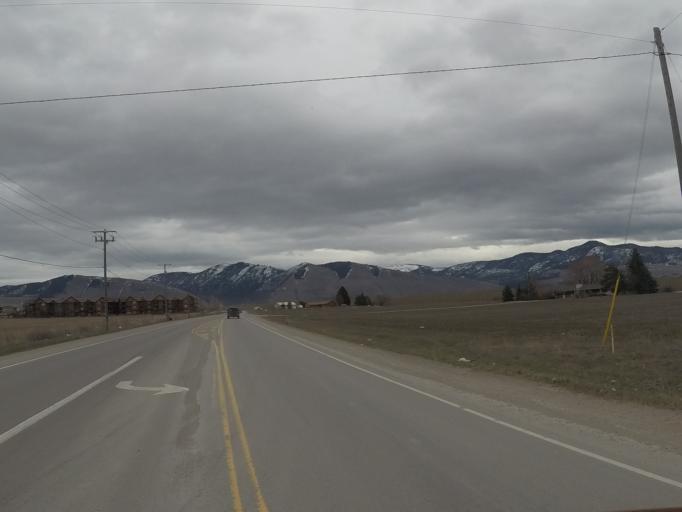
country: US
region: Montana
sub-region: Missoula County
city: Orchard Homes
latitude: 46.8876
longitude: -114.0553
